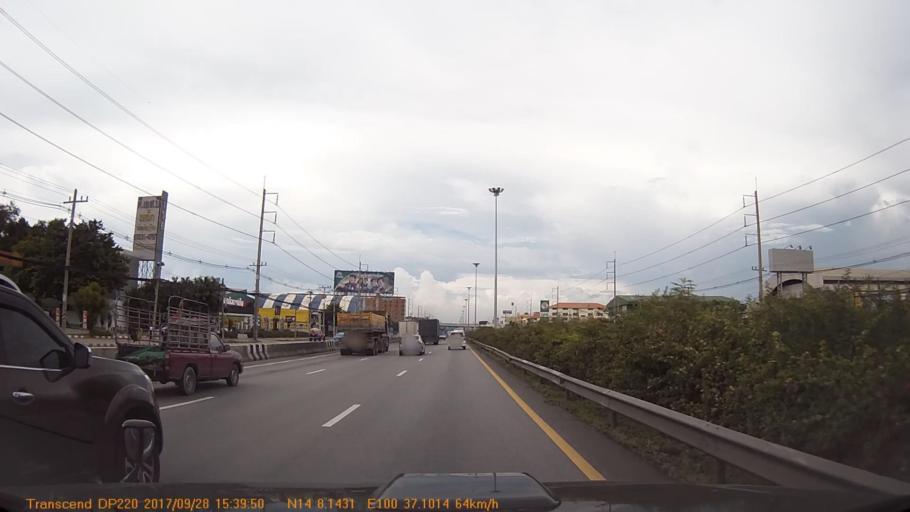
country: TH
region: Pathum Thani
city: Khlong Luang
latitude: 14.1360
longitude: 100.6184
